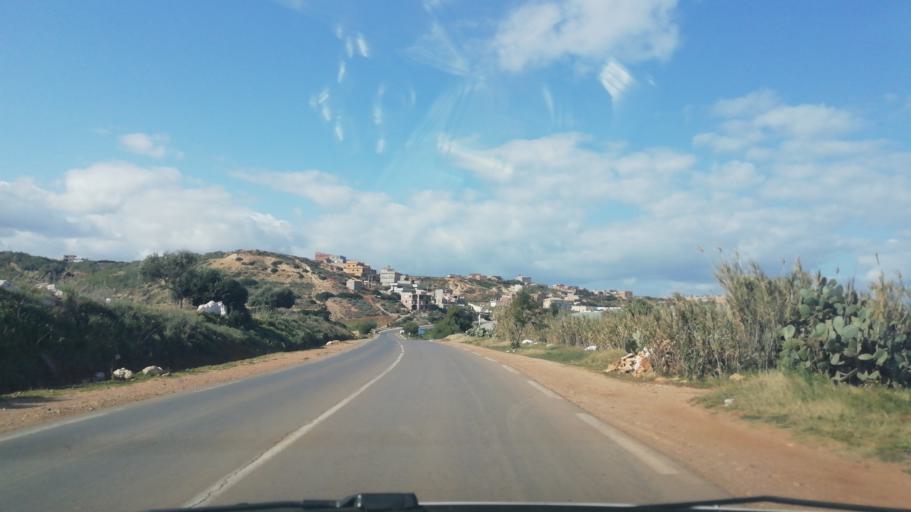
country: DZ
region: Relizane
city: Mazouna
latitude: 36.3267
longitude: 0.6997
